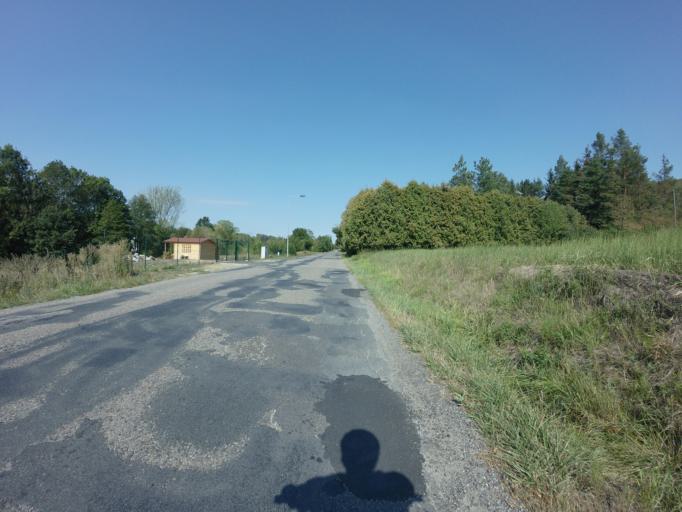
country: CZ
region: Central Bohemia
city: Tynec nad Sazavou
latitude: 49.8406
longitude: 14.5660
